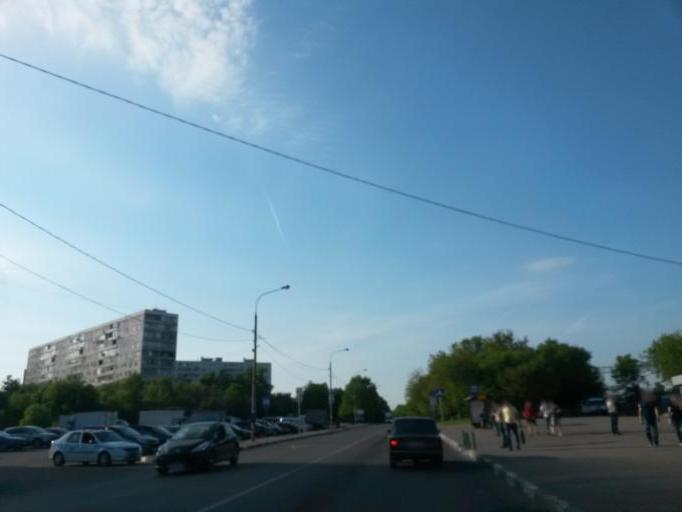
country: RU
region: Moscow
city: Zagor'ye
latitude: 55.5811
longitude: 37.6592
